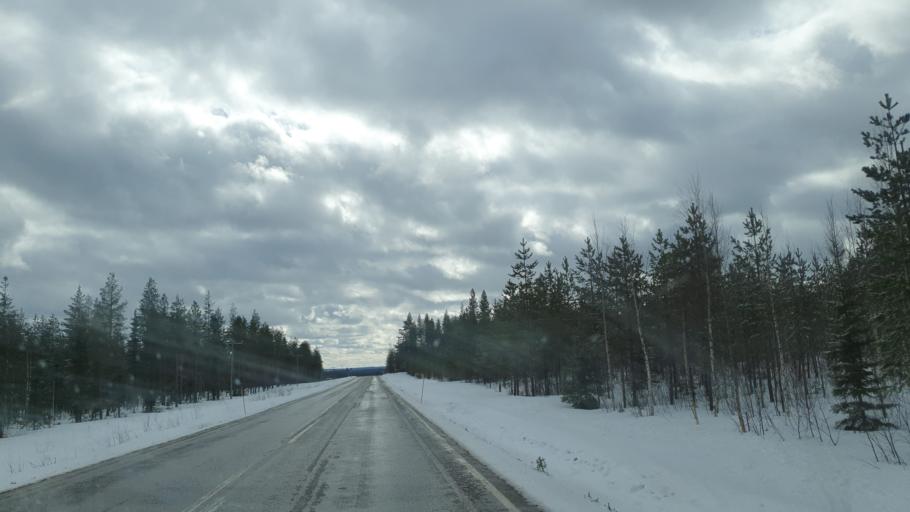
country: FI
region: Kainuu
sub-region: Kehys-Kainuu
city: Puolanka
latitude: 64.9504
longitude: 27.6010
